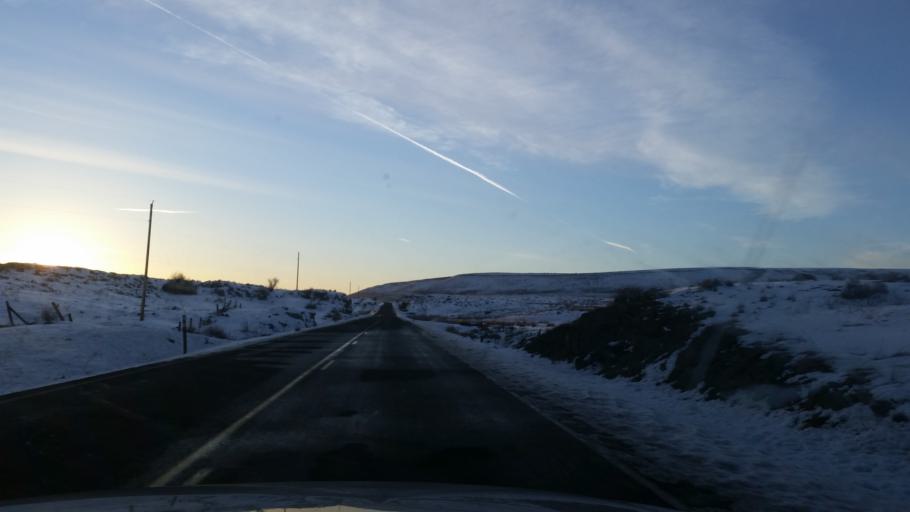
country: US
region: Washington
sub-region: Spokane County
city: Cheney
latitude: 47.1253
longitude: -117.7574
